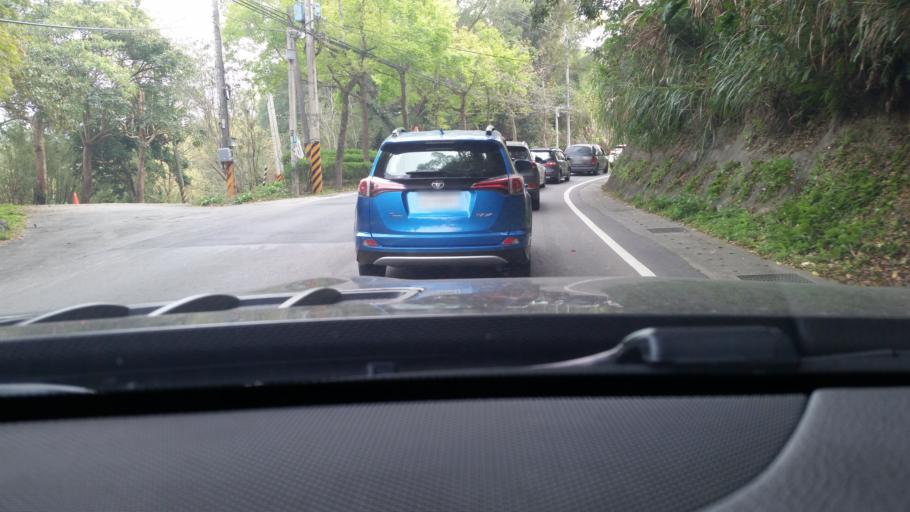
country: TW
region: Taiwan
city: Daxi
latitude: 24.8323
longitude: 121.3249
